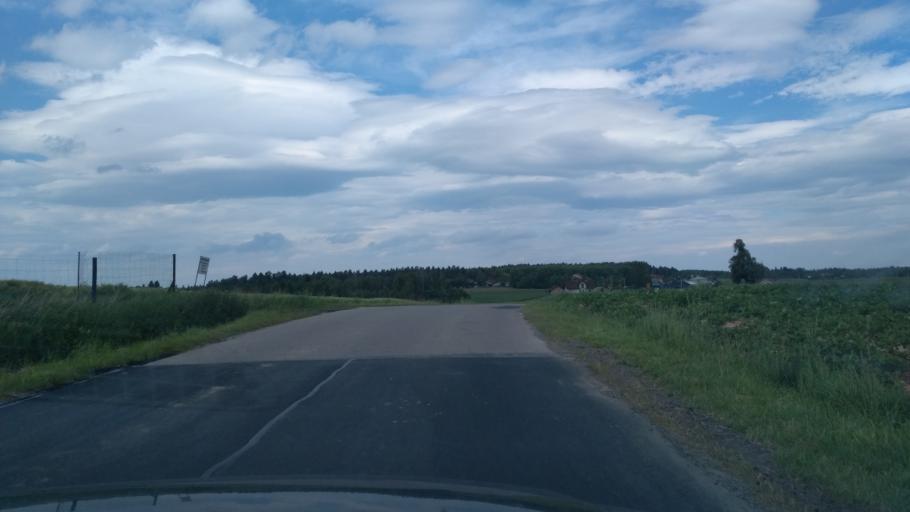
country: PL
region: Subcarpathian Voivodeship
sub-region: Powiat ropczycko-sedziszowski
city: Wielopole Skrzynskie
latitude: 49.9963
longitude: 21.6129
